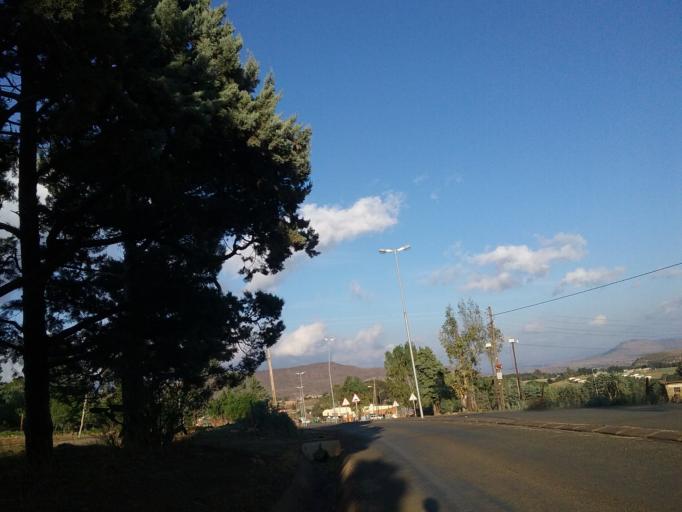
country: LS
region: Quthing
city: Quthing
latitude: -30.4079
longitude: 27.7047
